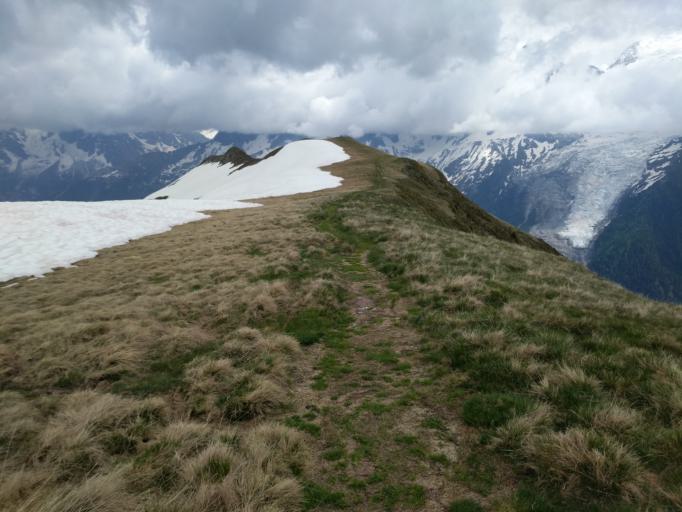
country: FR
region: Rhone-Alpes
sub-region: Departement de la Haute-Savoie
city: Les Houches
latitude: 45.9201
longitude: 6.8107
